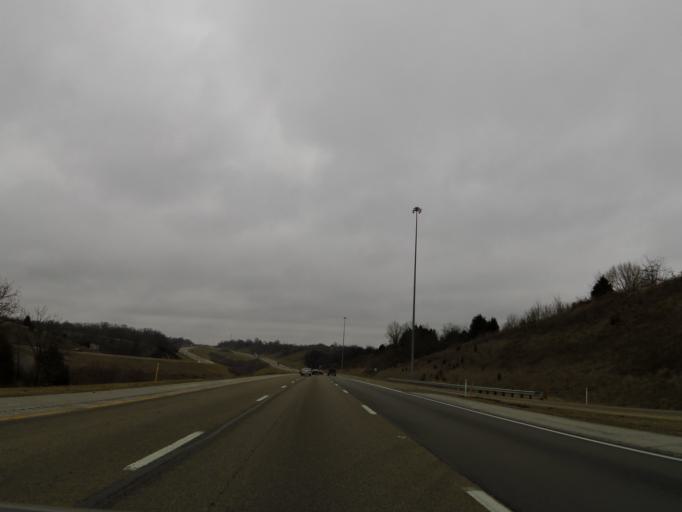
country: US
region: Kentucky
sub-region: Grant County
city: Williamstown
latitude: 38.6437
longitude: -84.5863
